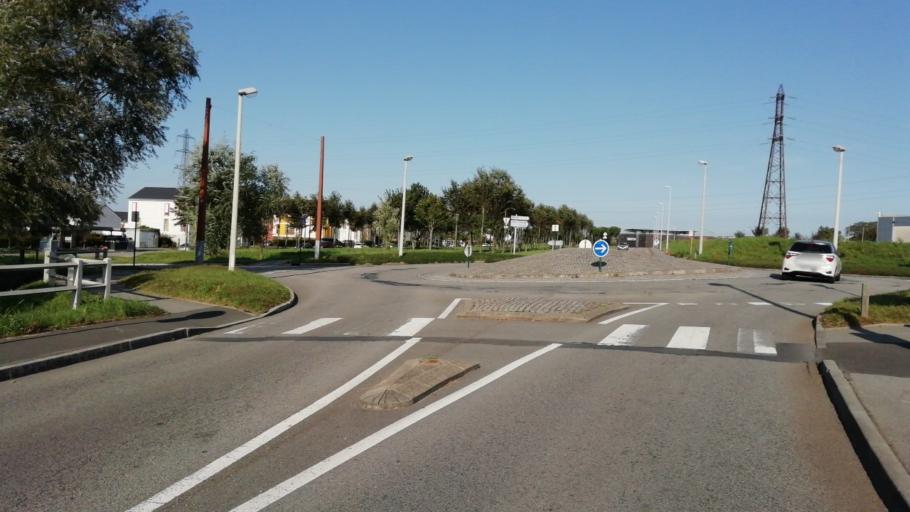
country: FR
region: Haute-Normandie
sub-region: Departement de la Seine-Maritime
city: Harfleur
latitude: 49.5041
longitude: 0.2247
